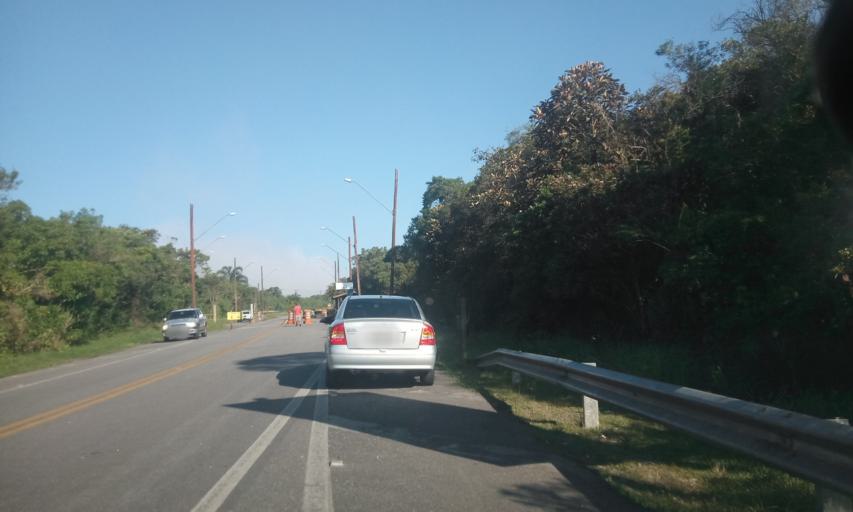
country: BR
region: Sao Paulo
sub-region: Cubatao
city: Cubatao
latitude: -23.8505
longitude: -46.4677
